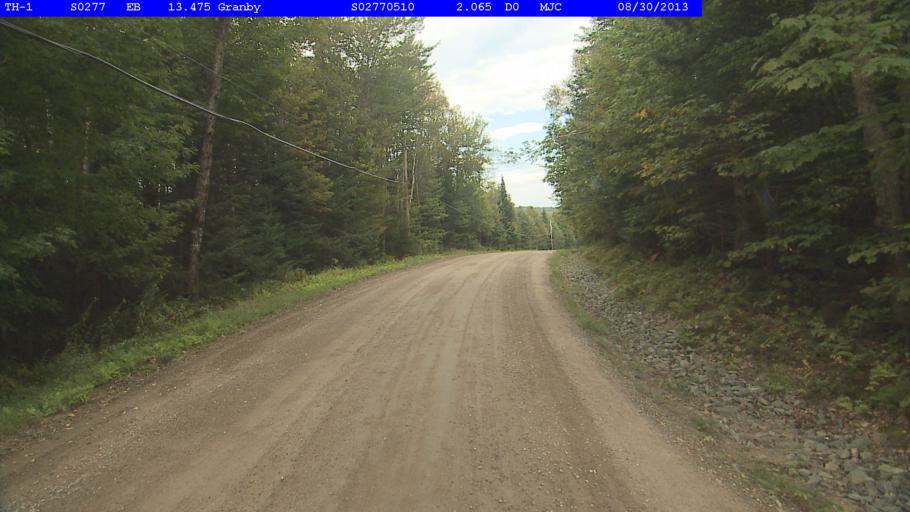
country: US
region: Vermont
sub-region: Essex County
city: Guildhall
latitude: 44.5780
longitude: -71.7253
